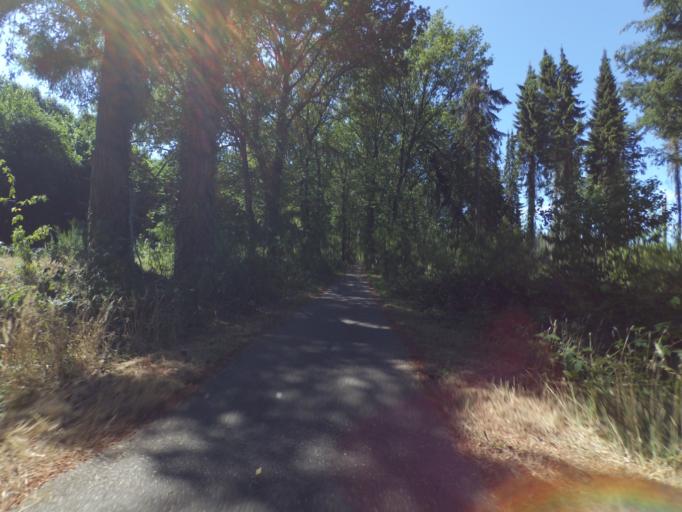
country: NL
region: Drenthe
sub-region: Gemeente Assen
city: Assen
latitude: 52.9266
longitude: 6.6596
